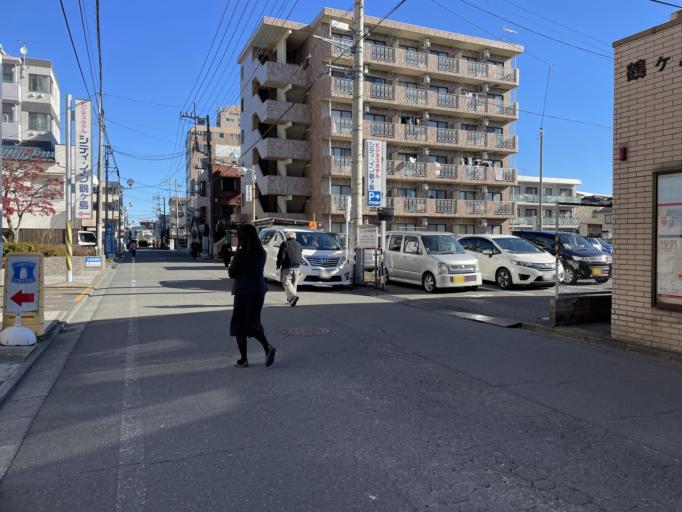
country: JP
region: Saitama
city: Sakado
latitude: 35.9382
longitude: 139.4244
